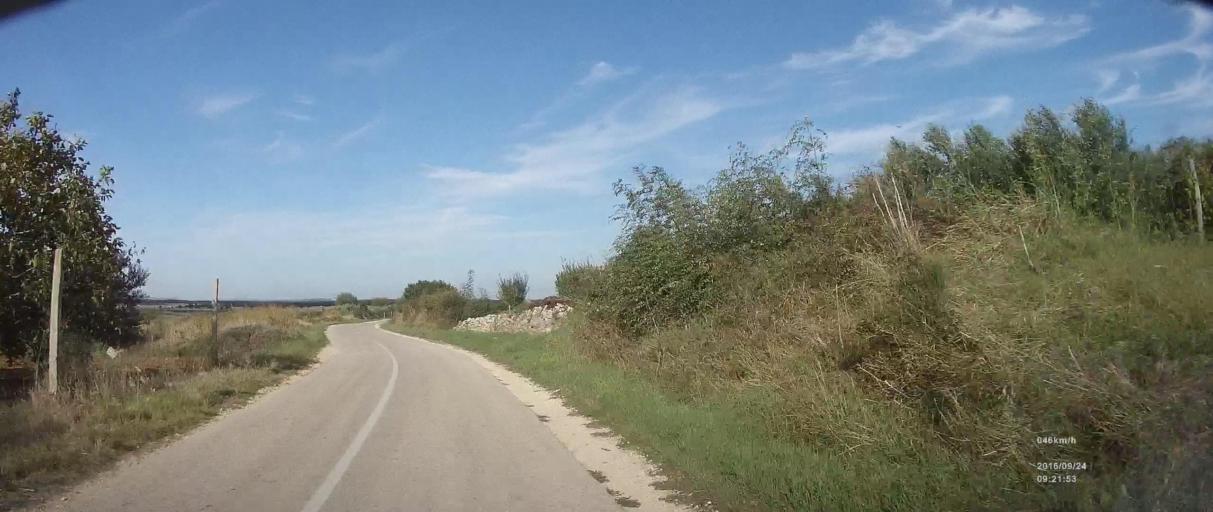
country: HR
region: Zadarska
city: Polaca
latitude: 44.0696
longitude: 15.4844
